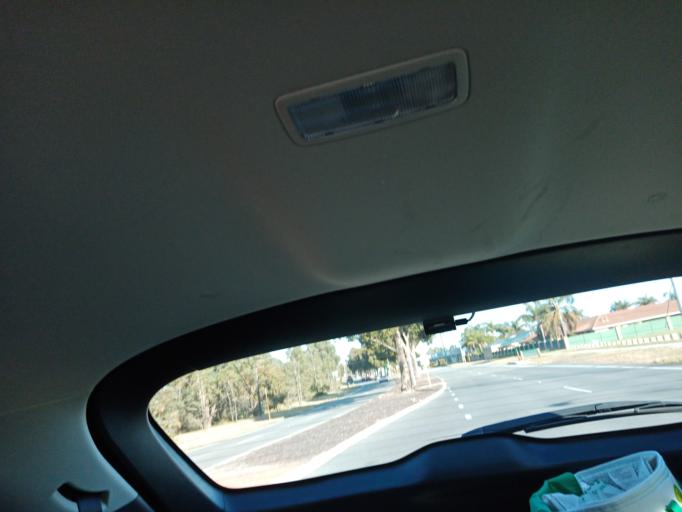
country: AU
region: Western Australia
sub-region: City of Cockburn
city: South Lake
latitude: -32.1172
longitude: 115.8401
